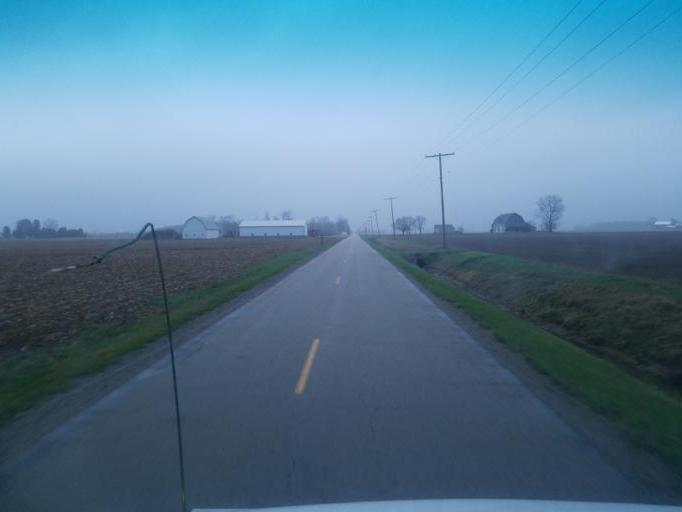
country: US
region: Ohio
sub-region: Fulton County
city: Archbold
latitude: 41.4277
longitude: -84.2753
